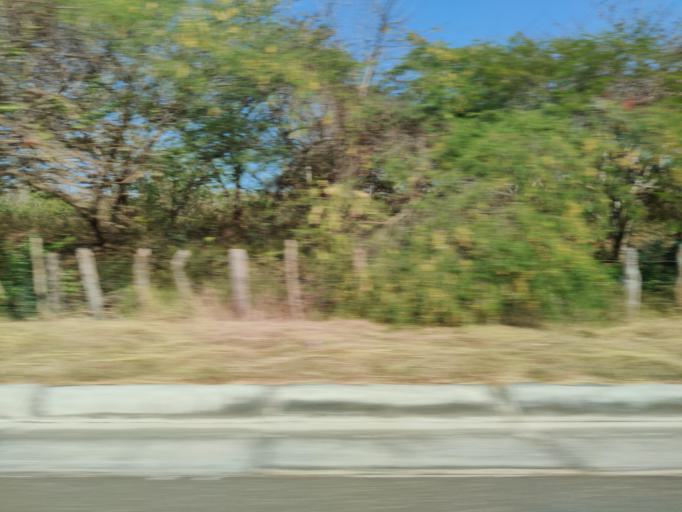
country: CO
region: Atlantico
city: Piojo
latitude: 10.8457
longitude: -75.1338
